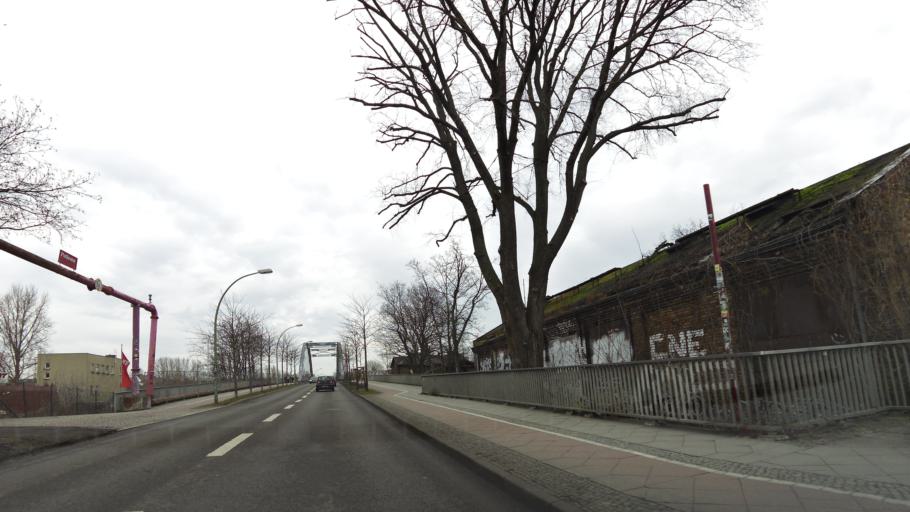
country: DE
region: Berlin
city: Friedrichshain Bezirk
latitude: 52.5038
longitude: 13.4575
